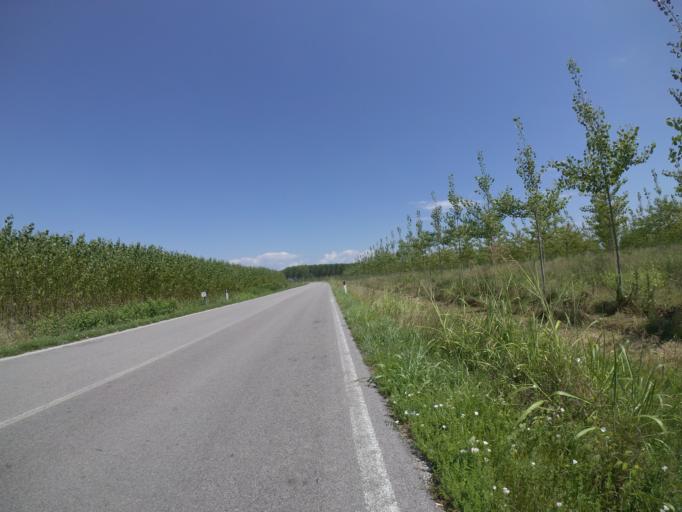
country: IT
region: Friuli Venezia Giulia
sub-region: Provincia di Udine
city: Talmassons
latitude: 45.8896
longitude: 13.1262
